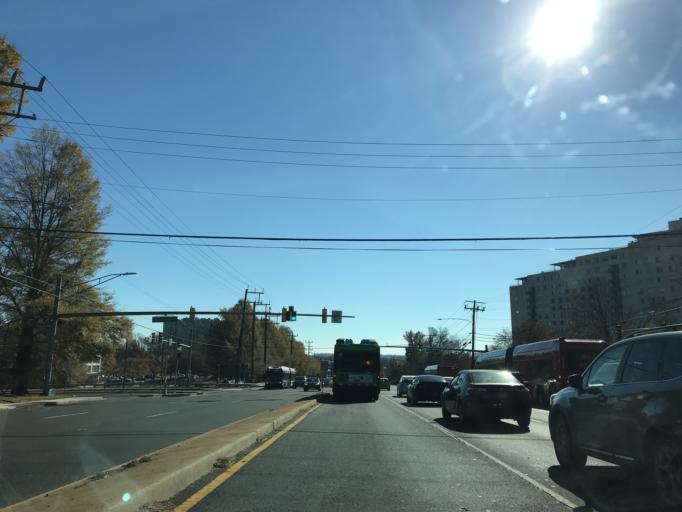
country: US
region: Maryland
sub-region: Montgomery County
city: North Bethesda
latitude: 39.0312
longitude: -77.1054
